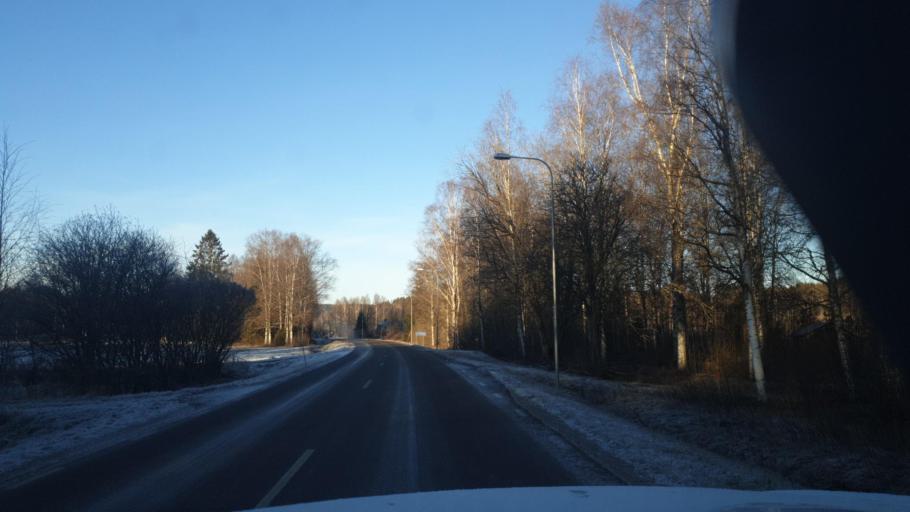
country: SE
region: Vaermland
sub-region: Arvika Kommun
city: Arvika
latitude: 59.6592
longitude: 12.8863
